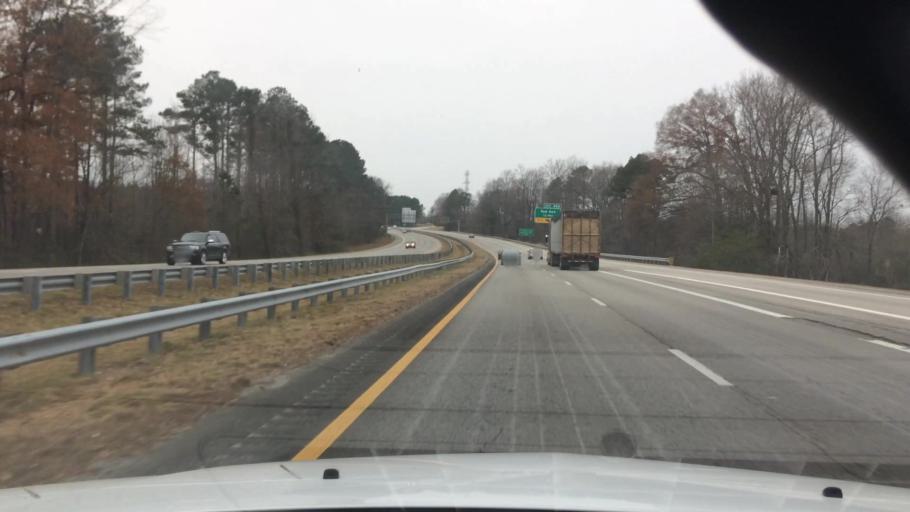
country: US
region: North Carolina
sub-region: Nash County
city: Red Oak
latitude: 35.9827
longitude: -77.8885
